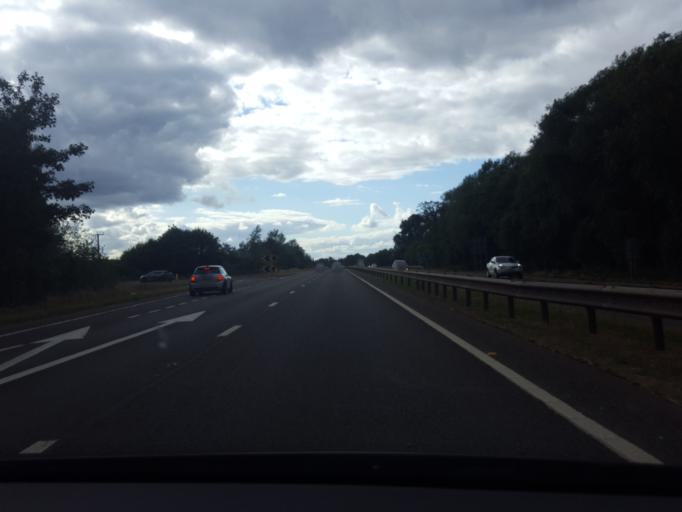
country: GB
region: England
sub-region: Leicestershire
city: Quorndon
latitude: 52.7509
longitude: -1.1674
